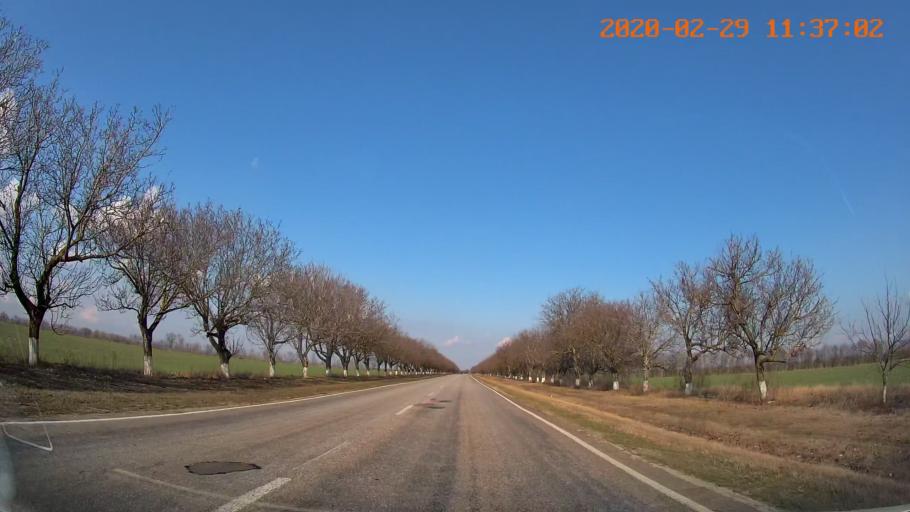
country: MD
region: Rezina
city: Saharna
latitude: 47.6056
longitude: 29.0496
